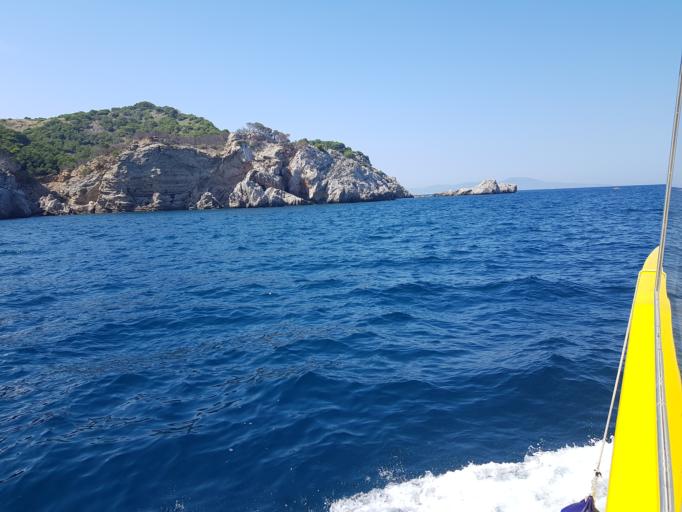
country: ES
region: Catalonia
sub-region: Provincia de Girona
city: Torroella de Montgri
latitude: 42.0568
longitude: 3.2139
